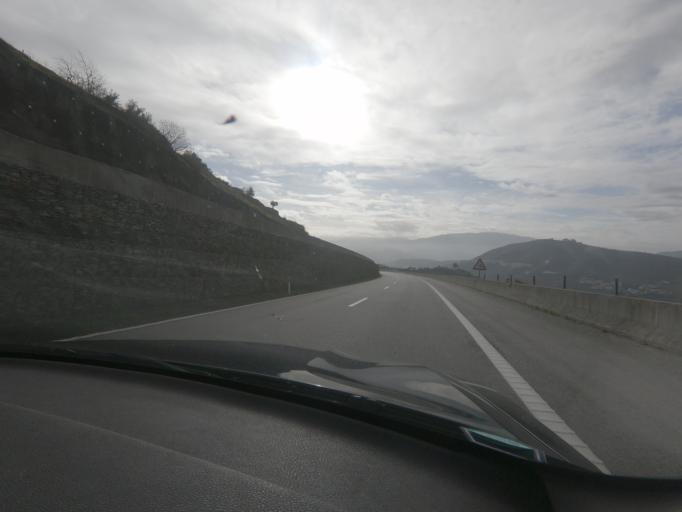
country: PT
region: Vila Real
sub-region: Peso da Regua
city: Peso da Regua
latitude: 41.1977
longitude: -7.7492
